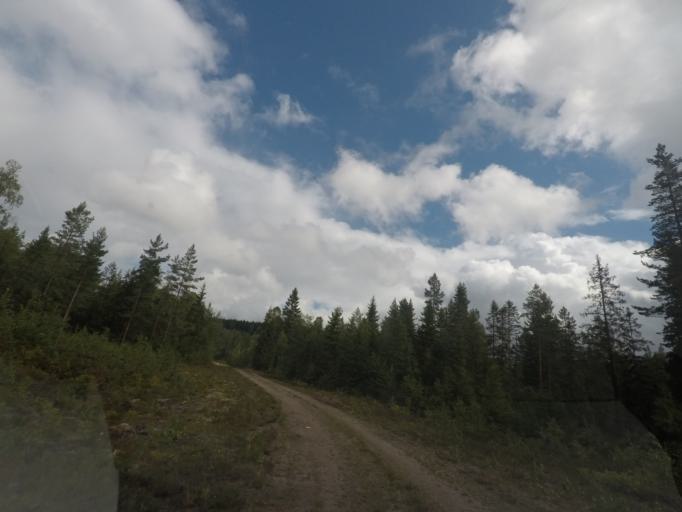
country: SE
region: Vaermland
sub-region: Filipstads Kommun
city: Lesjofors
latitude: 60.1047
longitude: 14.3891
